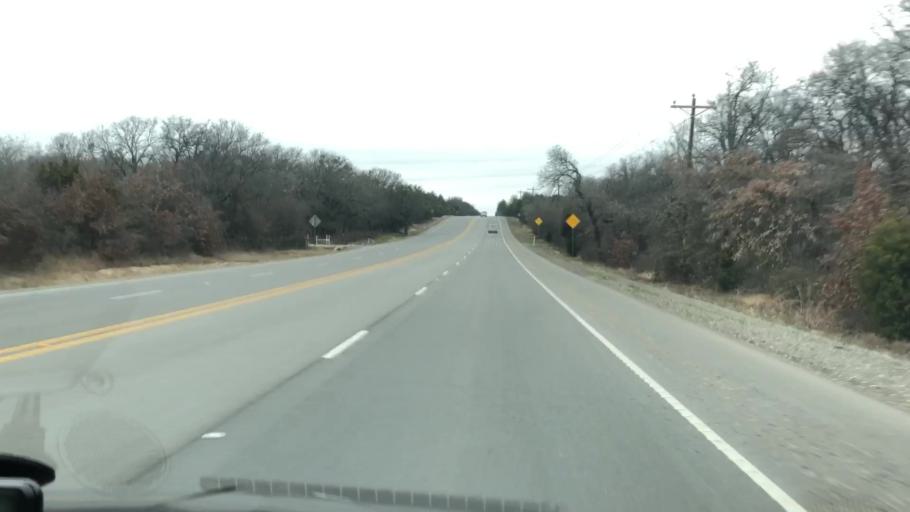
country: US
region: Texas
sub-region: Hamilton County
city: Hico
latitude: 32.1021
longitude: -98.1111
